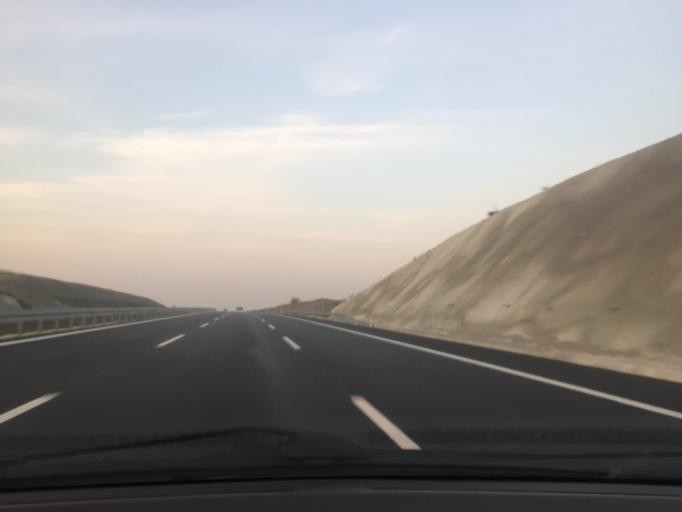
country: TR
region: Bursa
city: Karacabey
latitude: 40.2712
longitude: 28.5008
